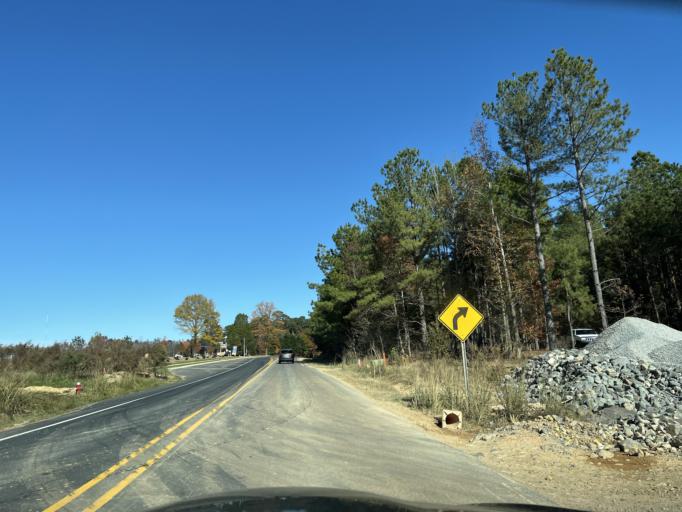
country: US
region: North Carolina
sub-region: Wake County
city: Garner
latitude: 35.6626
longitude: -78.7166
